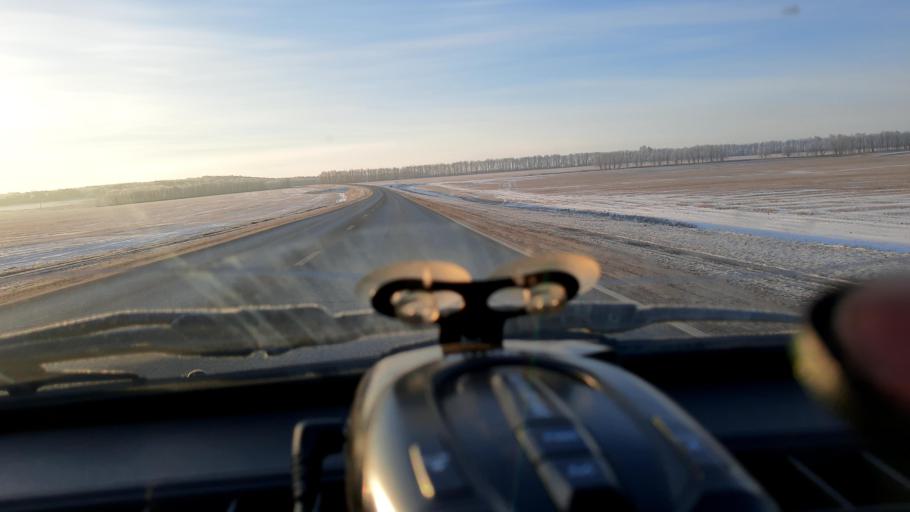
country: RU
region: Bashkortostan
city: Mikhaylovka
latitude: 54.8642
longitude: 55.7047
